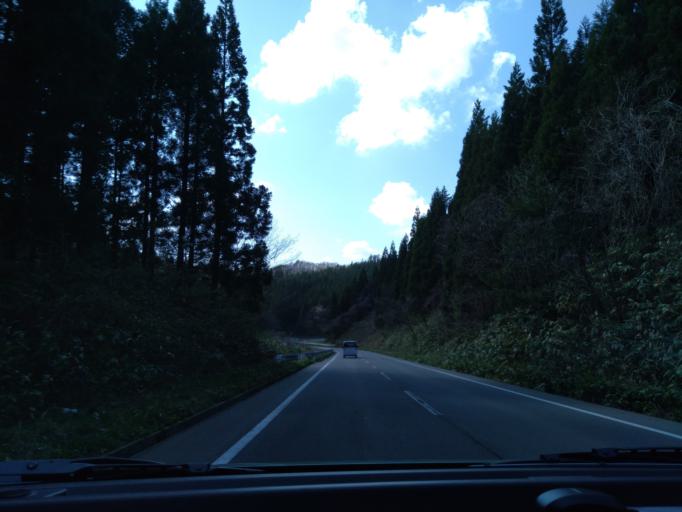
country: JP
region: Akita
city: Akita
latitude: 39.6949
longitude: 140.2387
